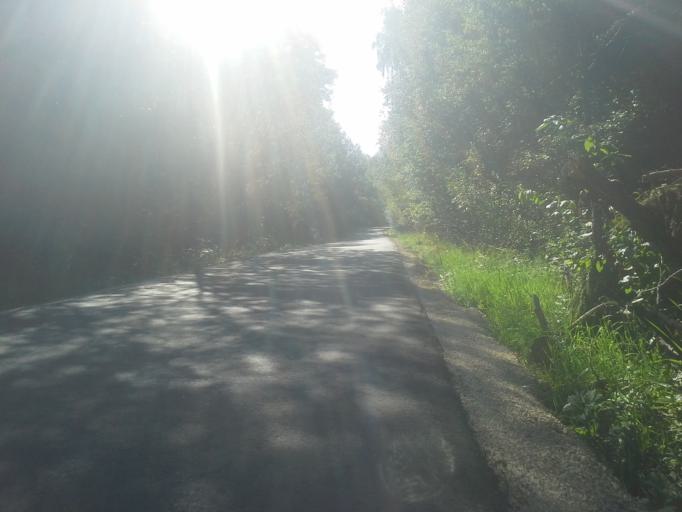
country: RU
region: Moskovskaya
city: Kievskij
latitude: 55.3317
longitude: 36.9920
